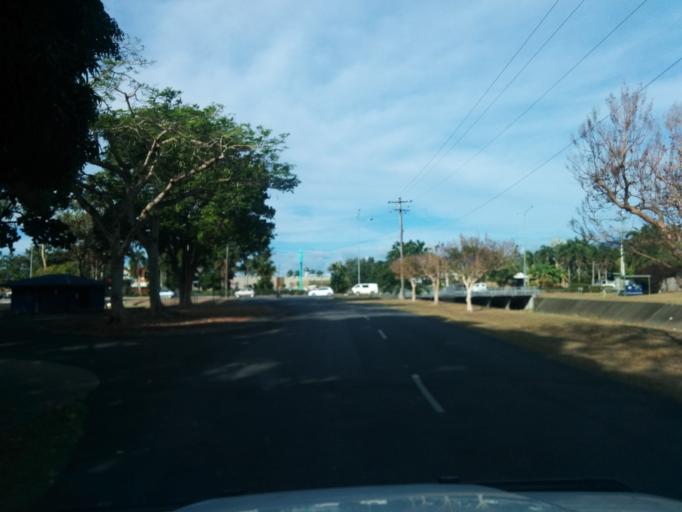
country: AU
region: Queensland
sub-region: Cairns
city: Woree
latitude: -16.9468
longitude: 145.7377
